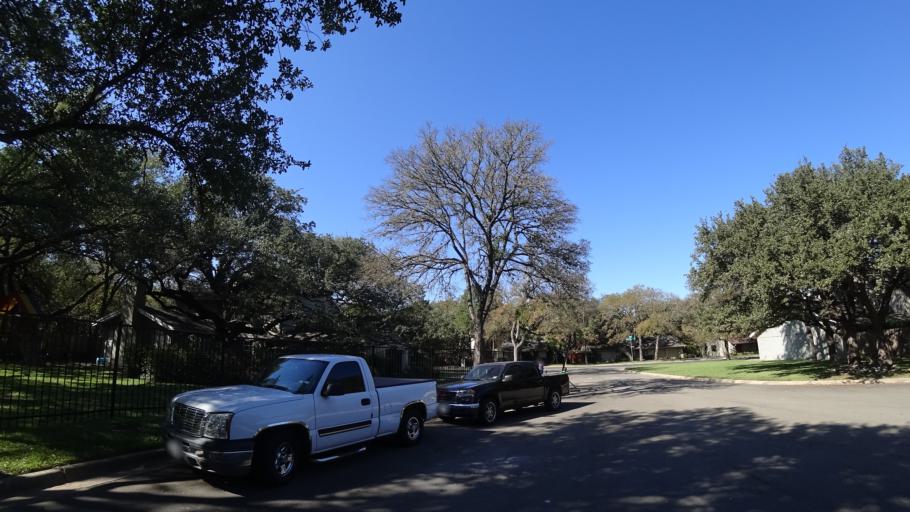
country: US
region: Texas
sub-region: Williamson County
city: Jollyville
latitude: 30.3840
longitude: -97.7480
